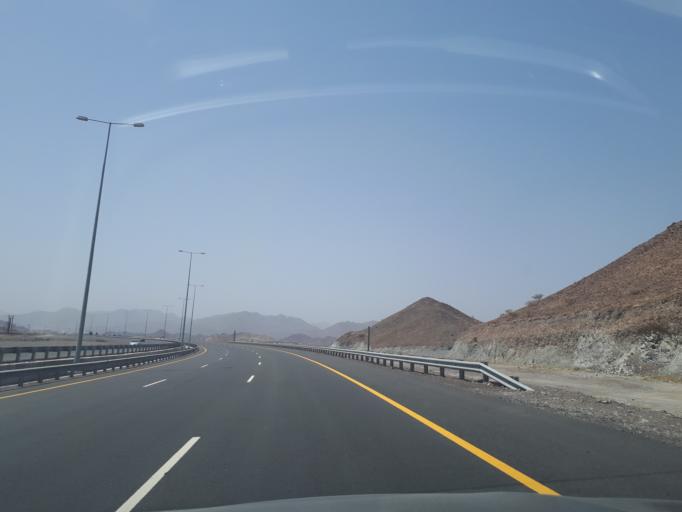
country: OM
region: Muhafazat ad Dakhiliyah
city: Sufalat Sama'il
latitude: 23.3110
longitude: 58.1100
